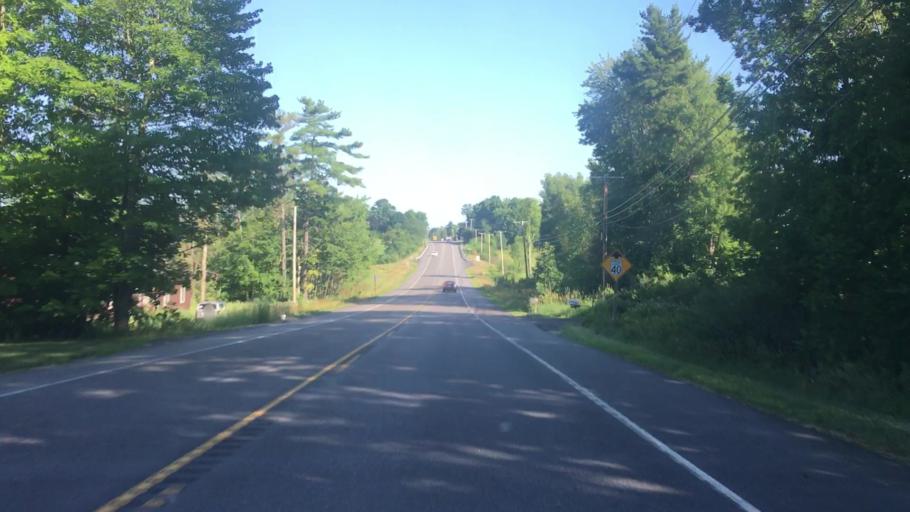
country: US
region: Maine
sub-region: Cumberland County
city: Gorham
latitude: 43.6975
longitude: -70.4960
